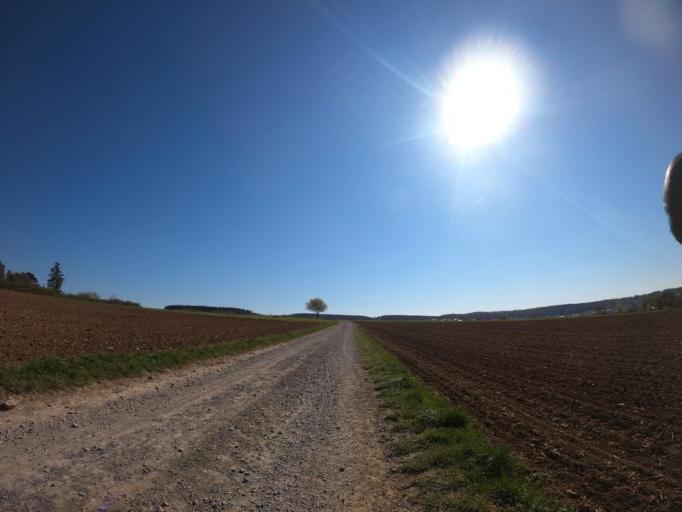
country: DE
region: Baden-Wuerttemberg
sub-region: Karlsruhe Region
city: Wiernsheim
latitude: 48.8935
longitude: 8.8666
